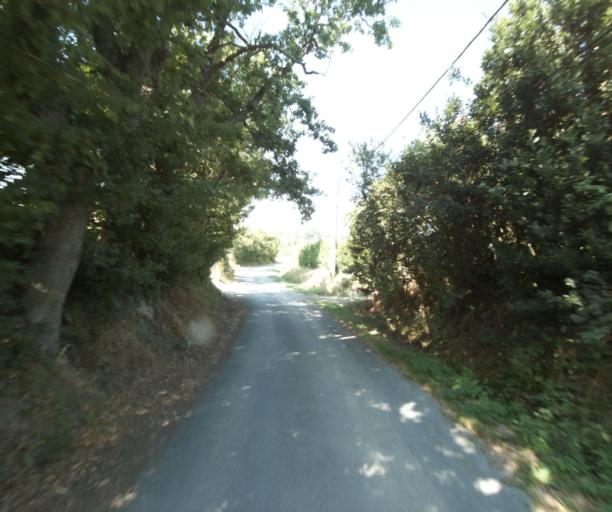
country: FR
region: Midi-Pyrenees
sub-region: Departement de la Haute-Garonne
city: Revel
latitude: 43.4840
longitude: 1.9967
